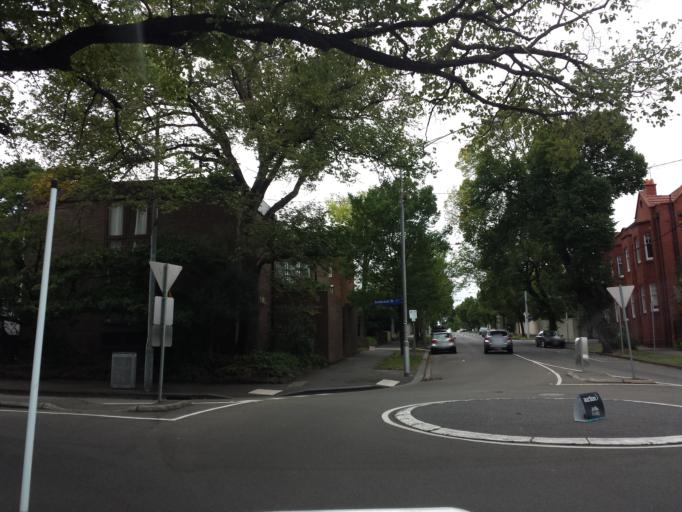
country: AU
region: Victoria
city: Albert Park
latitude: -37.8342
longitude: 144.9836
